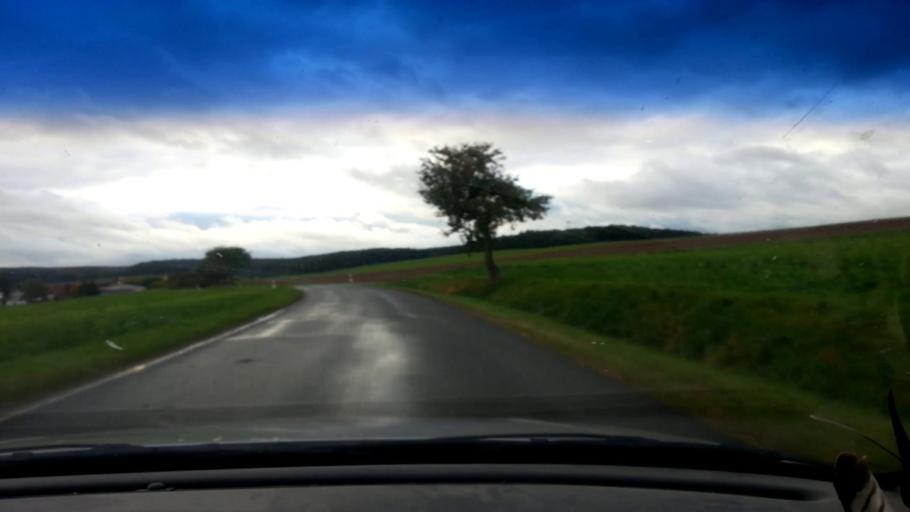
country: DE
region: Bavaria
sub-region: Upper Franconia
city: Burgwindheim
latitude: 49.8100
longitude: 10.6488
